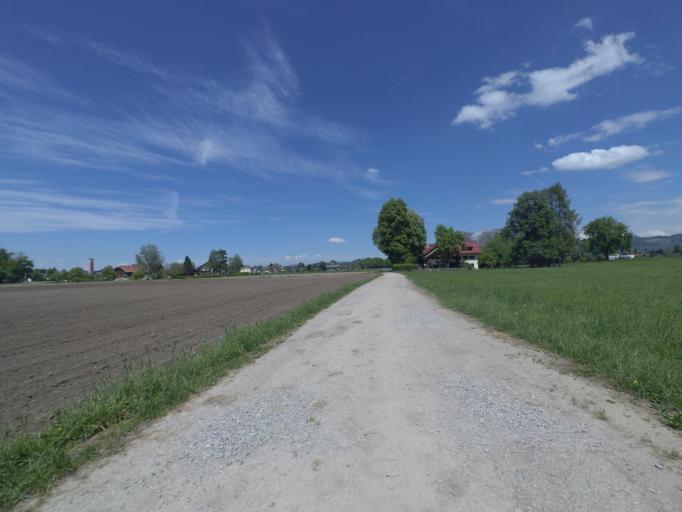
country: AT
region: Salzburg
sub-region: Politischer Bezirk Salzburg-Umgebung
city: Anif
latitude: 47.7687
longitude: 13.0462
